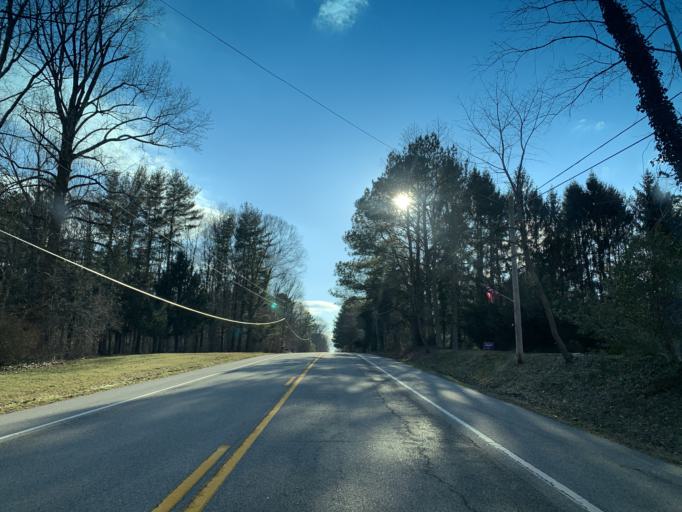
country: US
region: Maryland
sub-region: Queen Anne's County
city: Kingstown
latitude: 39.1545
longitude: -75.9582
